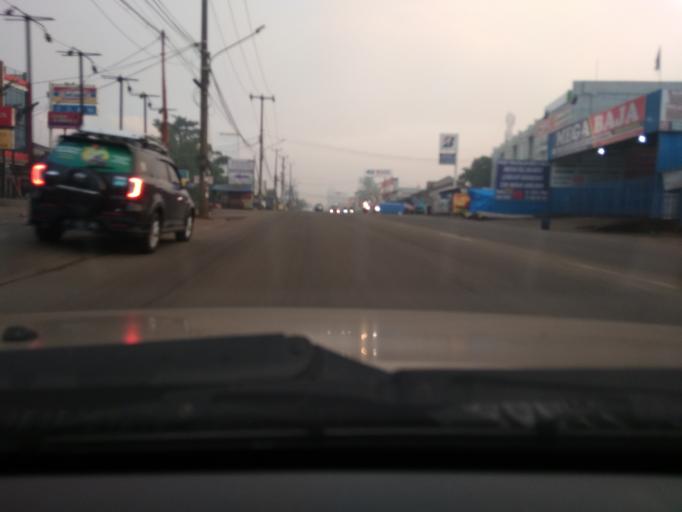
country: ID
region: West Java
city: Serpong
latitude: -6.3262
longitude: 106.6842
